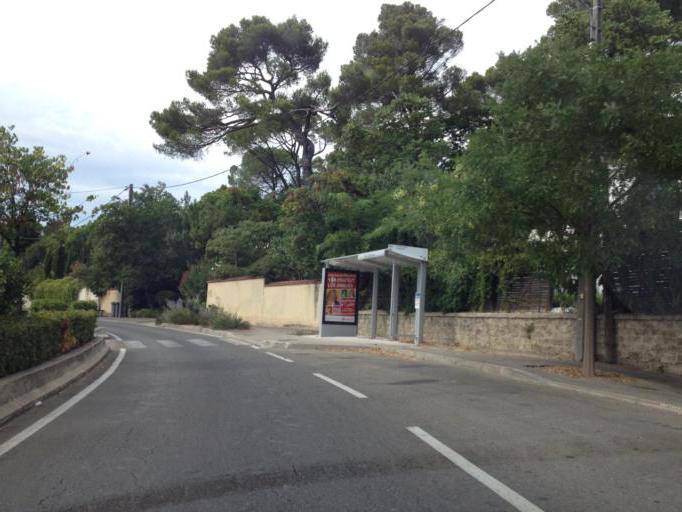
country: FR
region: Languedoc-Roussillon
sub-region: Departement du Gard
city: Villeneuve-les-Avignon
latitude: 43.9560
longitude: 4.7841
